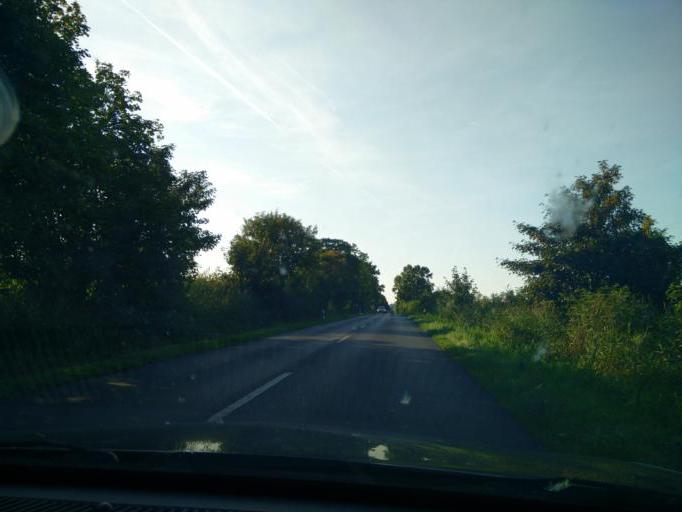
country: HU
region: Pest
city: Zsambek
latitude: 47.5190
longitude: 18.7495
